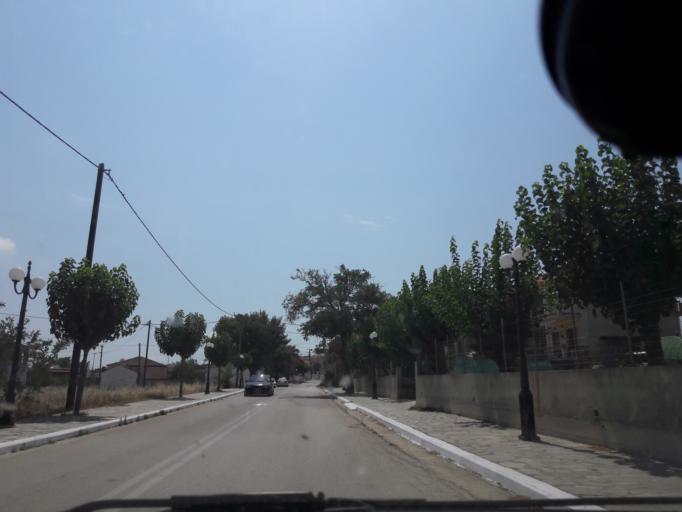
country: GR
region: North Aegean
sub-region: Nomos Lesvou
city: Myrina
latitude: 39.9293
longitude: 25.3363
